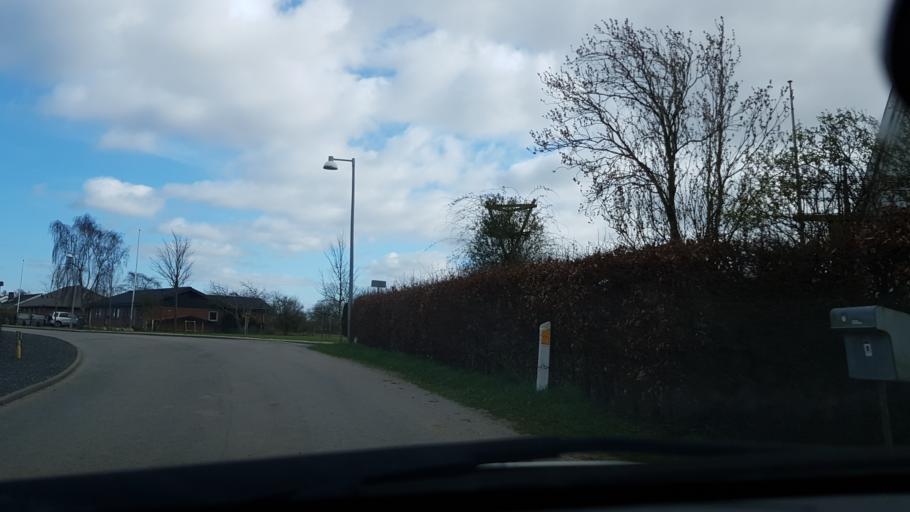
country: DK
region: South Denmark
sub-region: Vejen Kommune
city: Rodding
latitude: 55.4217
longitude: 9.0942
